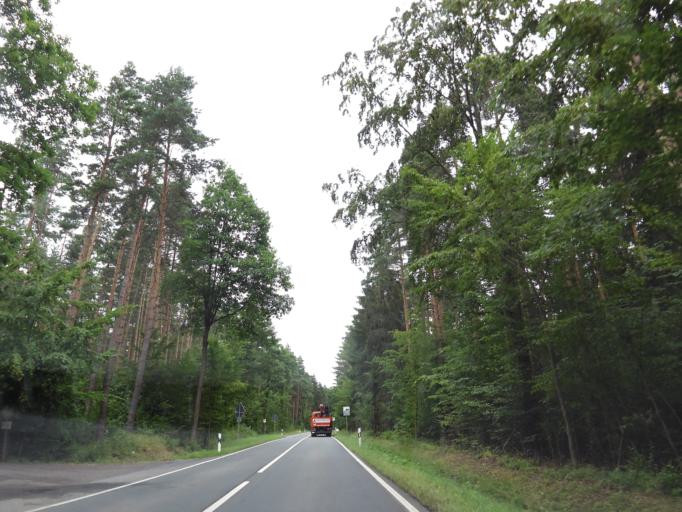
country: DE
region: Thuringia
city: Hainspitz
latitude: 50.9405
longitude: 11.8519
